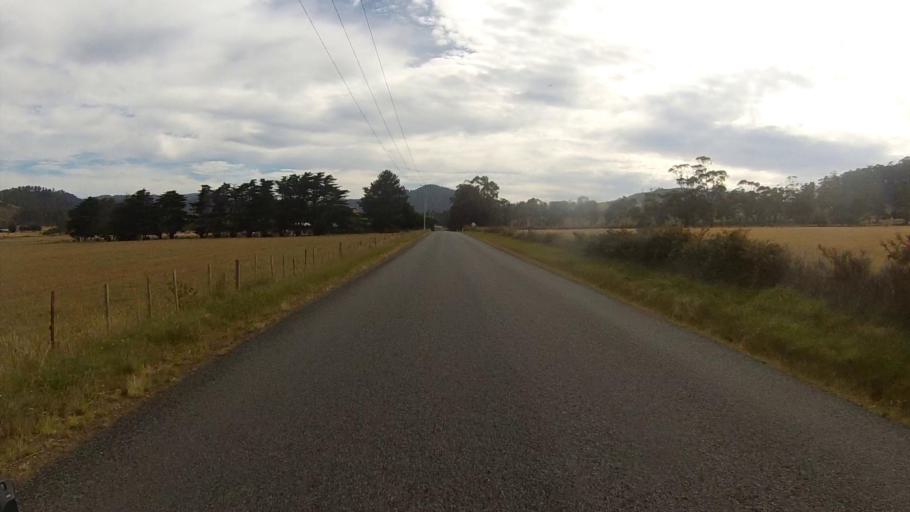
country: AU
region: Tasmania
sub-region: Sorell
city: Sorell
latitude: -42.7947
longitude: 147.7956
